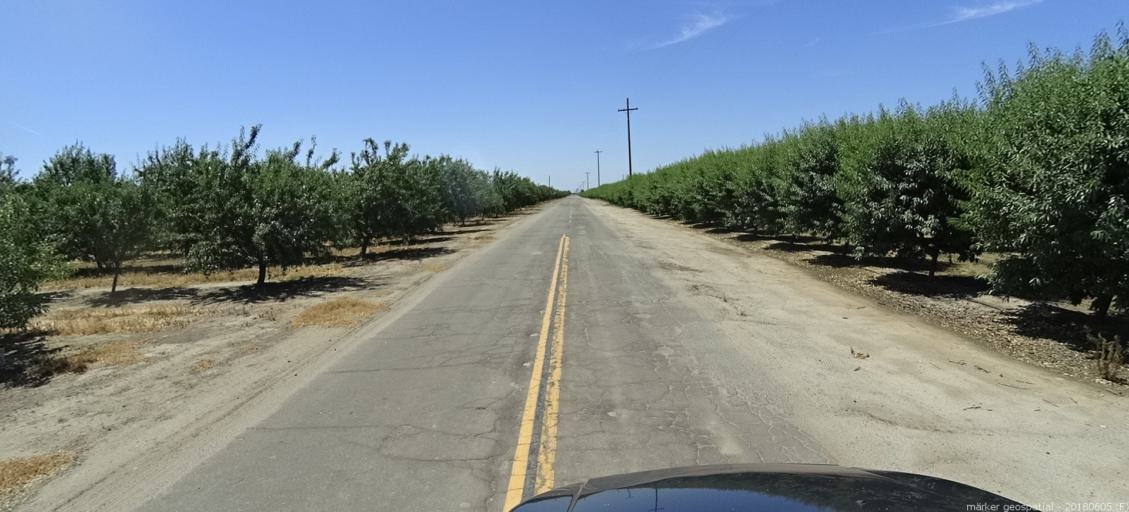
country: US
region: California
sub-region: Madera County
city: Chowchilla
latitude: 37.0979
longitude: -120.4553
